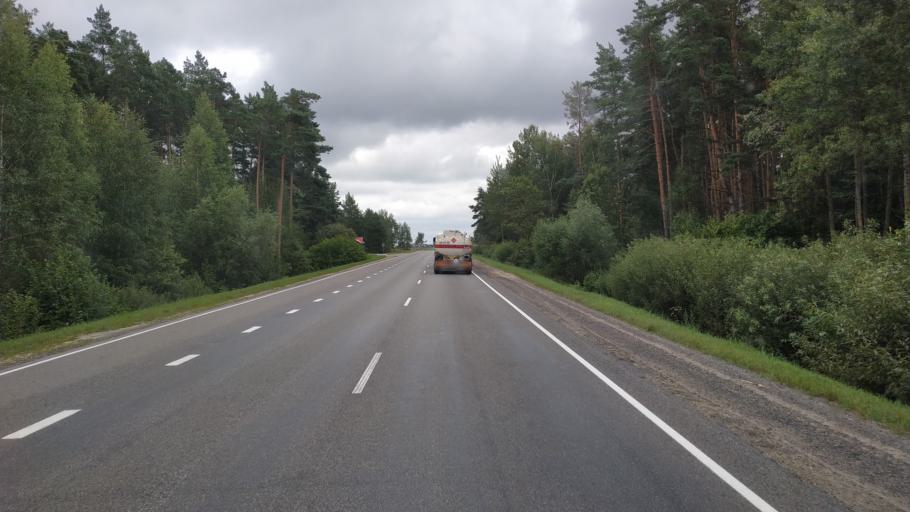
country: BY
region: Mogilev
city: Chavusy
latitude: 53.8038
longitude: 30.9260
